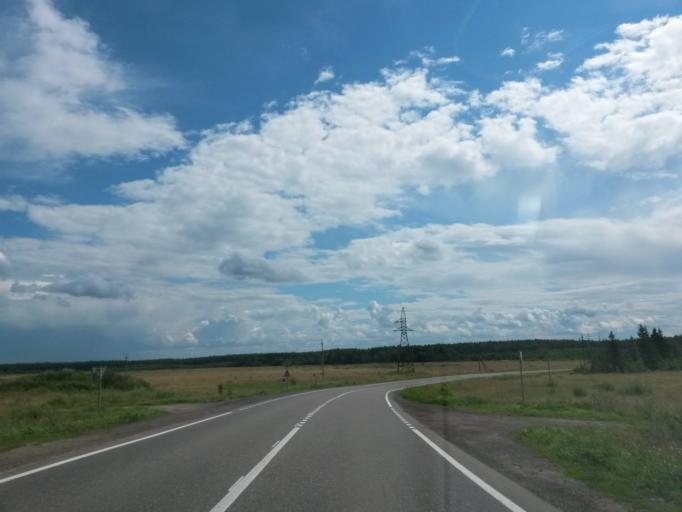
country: RU
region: Jaroslavl
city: Gavrilov-Yam
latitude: 57.3040
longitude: 39.9461
